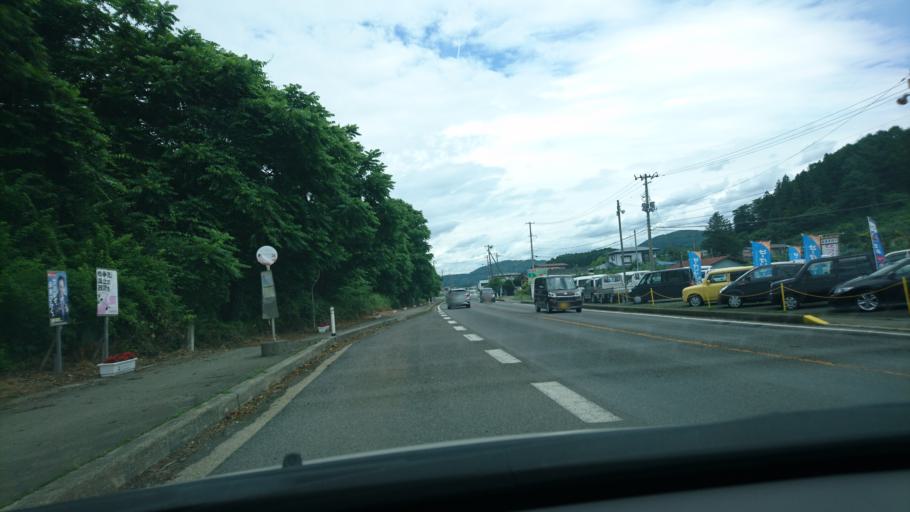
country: JP
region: Iwate
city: Morioka-shi
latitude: 39.6251
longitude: 141.1833
